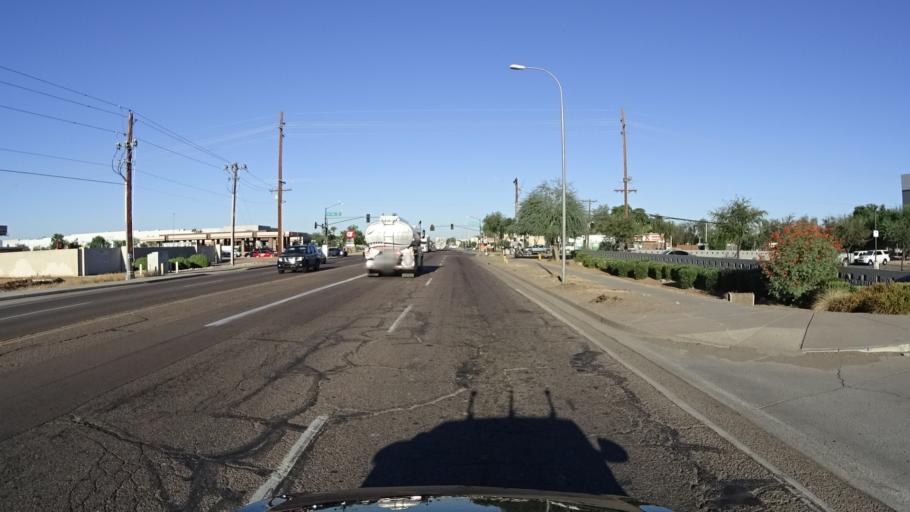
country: US
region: Arizona
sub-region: Maricopa County
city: Tolleson
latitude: 33.4373
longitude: -112.2026
